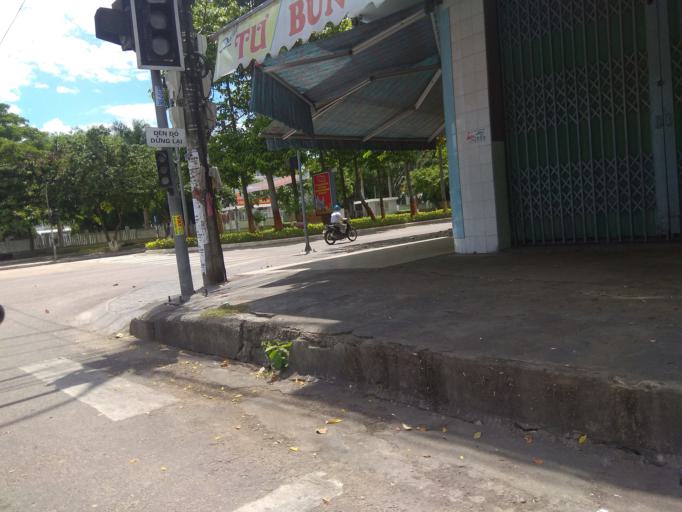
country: VN
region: Quang Nam
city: Tam Ky
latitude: 15.5716
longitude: 108.4732
